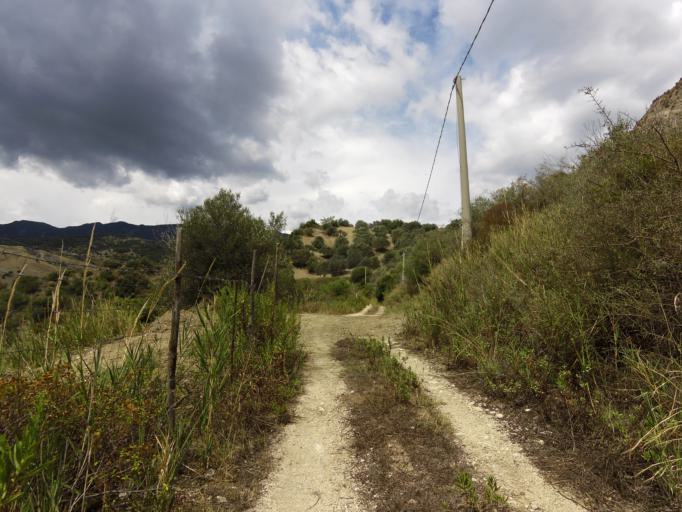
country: IT
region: Calabria
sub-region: Provincia di Reggio Calabria
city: Camini
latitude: 38.4522
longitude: 16.4750
